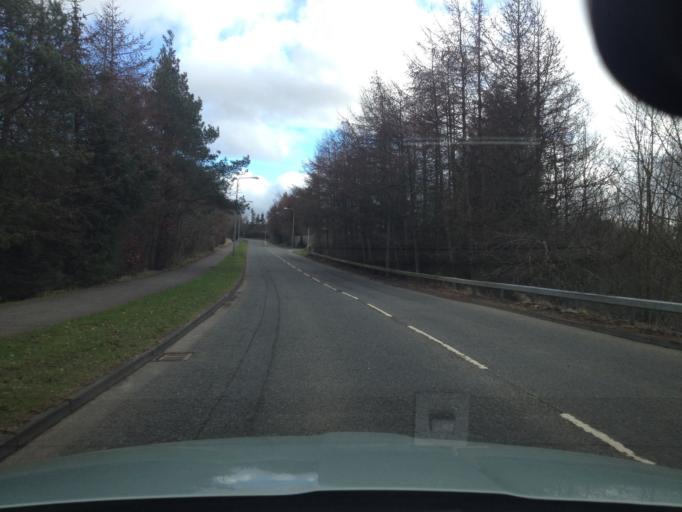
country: GB
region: Scotland
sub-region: West Lothian
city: Livingston
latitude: 55.8592
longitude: -3.5181
